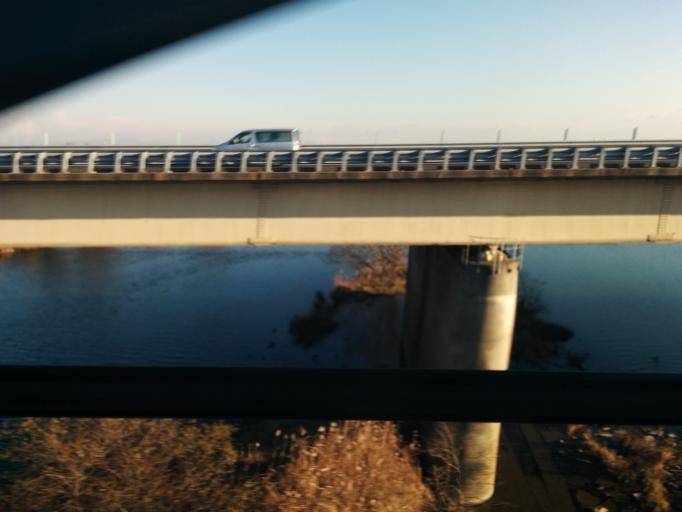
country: JP
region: Aichi
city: Sobue
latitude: 35.2963
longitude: 136.7223
